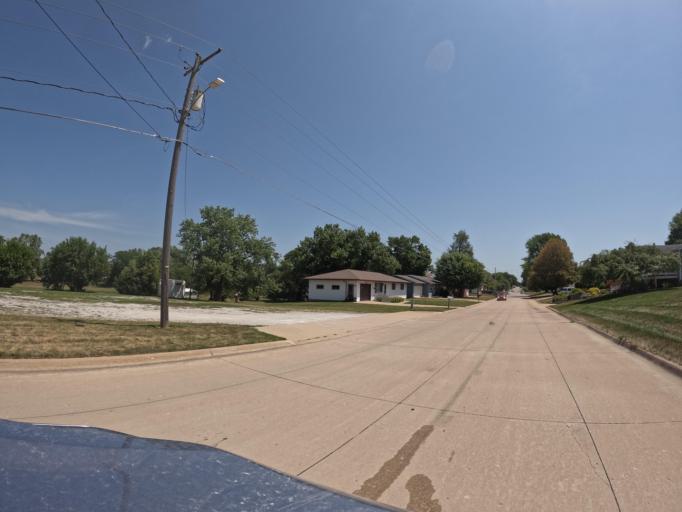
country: US
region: Iowa
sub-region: Henry County
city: Mount Pleasant
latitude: 40.9559
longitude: -91.5559
